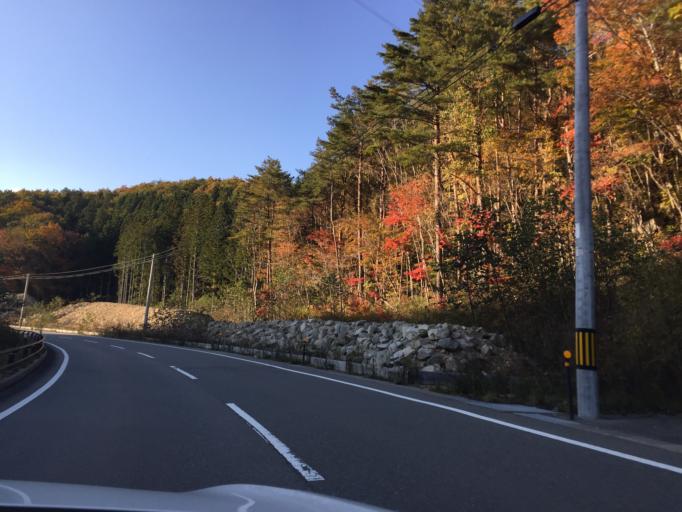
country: JP
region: Fukushima
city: Funehikimachi-funehiki
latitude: 37.2913
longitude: 140.7511
